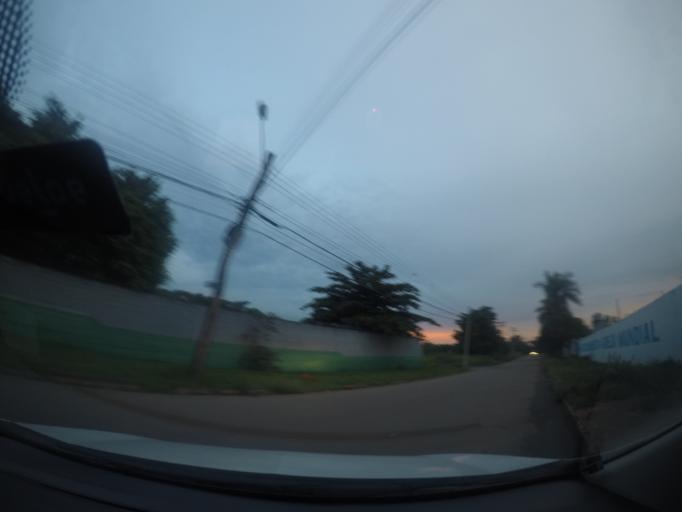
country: BR
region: Goias
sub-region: Goiania
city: Goiania
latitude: -16.6422
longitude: -49.2441
